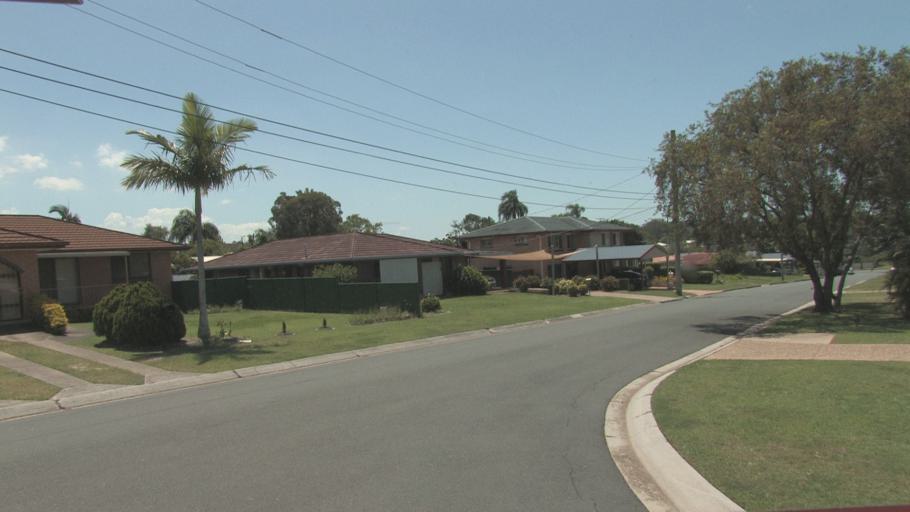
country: AU
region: Queensland
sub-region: Logan
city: Rochedale South
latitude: -27.5976
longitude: 153.1233
